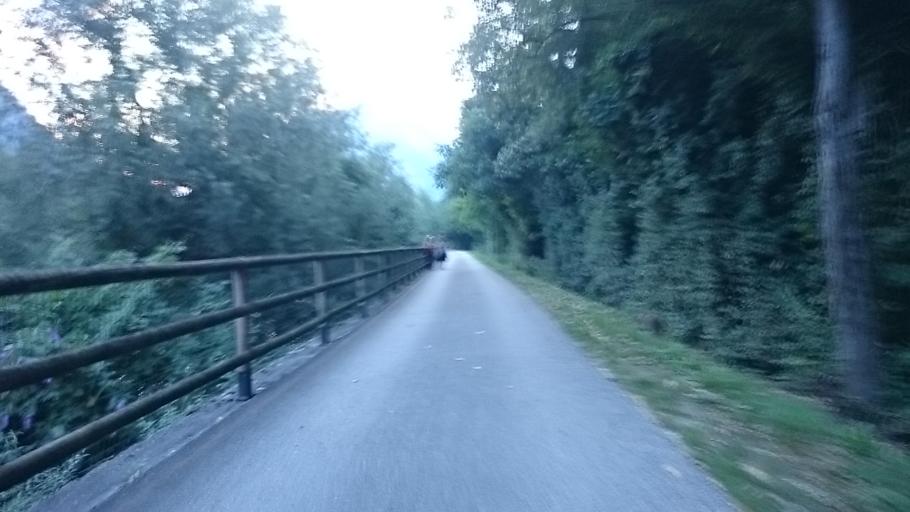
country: IT
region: Trentino-Alto Adige
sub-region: Provincia di Trento
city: Grigno
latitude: 45.9962
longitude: 11.6628
